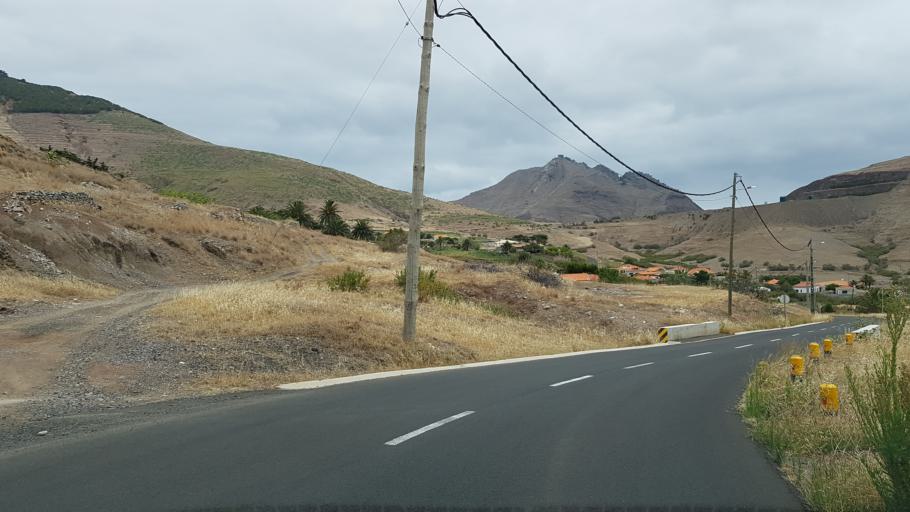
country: PT
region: Madeira
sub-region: Porto Santo
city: Vila de Porto Santo
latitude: 33.0707
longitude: -16.3148
